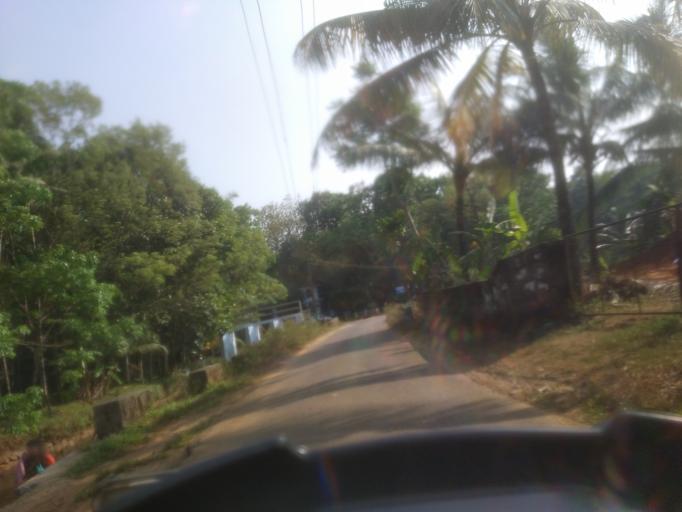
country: IN
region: Kerala
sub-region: Ernakulam
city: Piravam
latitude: 9.8787
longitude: 76.5539
